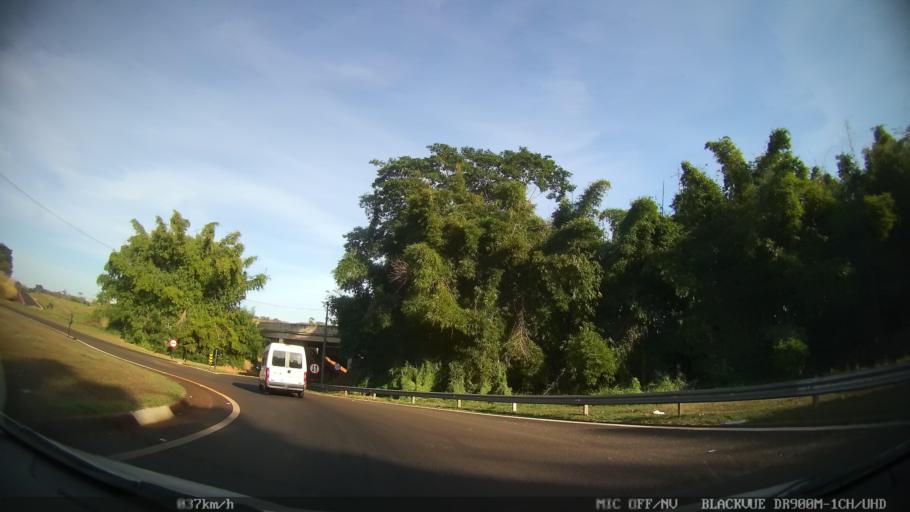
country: BR
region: Sao Paulo
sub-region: Cravinhos
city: Cravinhos
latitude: -21.2916
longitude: -47.8114
